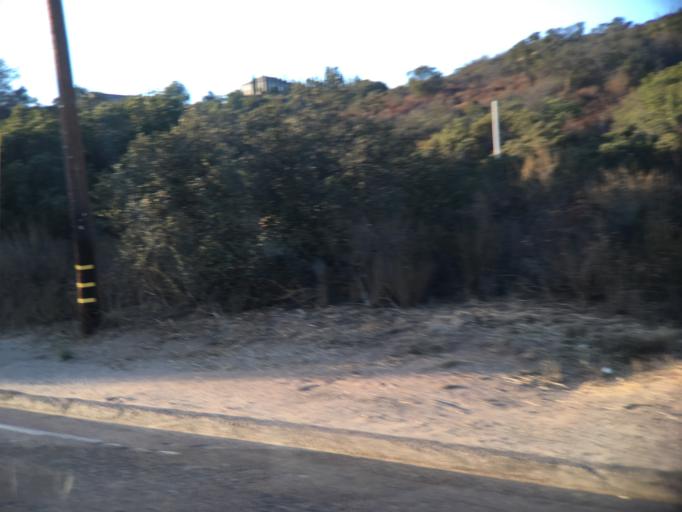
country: US
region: California
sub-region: San Diego County
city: Alpine
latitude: 32.8033
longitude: -116.7756
